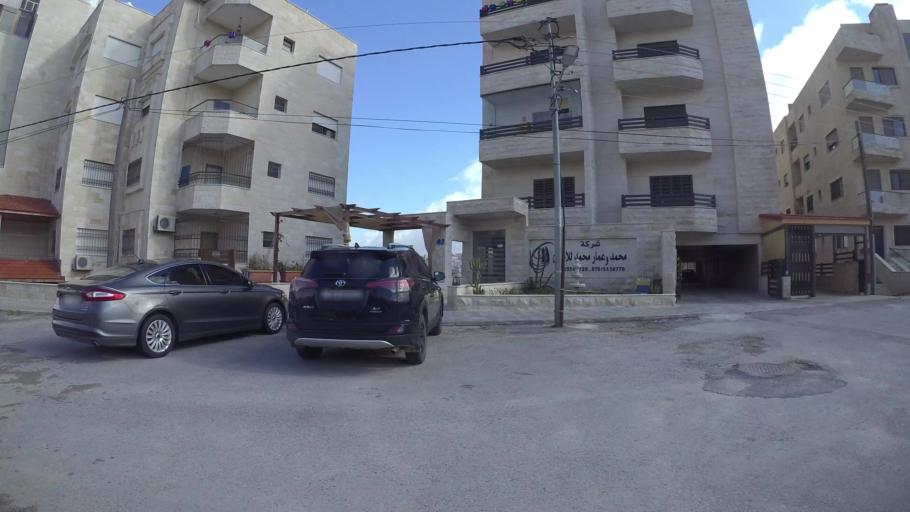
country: JO
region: Amman
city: Al Jubayhah
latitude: 32.0395
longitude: 35.8748
